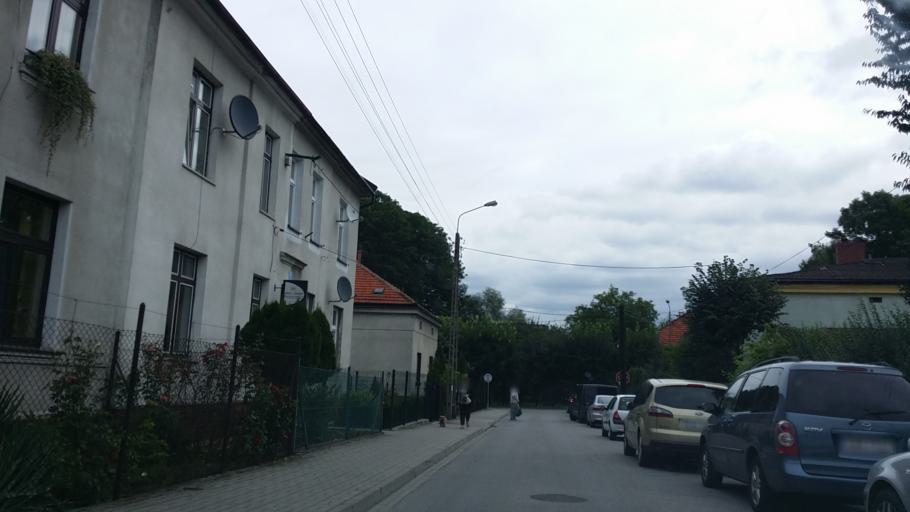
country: PL
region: Lesser Poland Voivodeship
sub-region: Powiat wadowicki
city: Wadowice
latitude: 49.8845
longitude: 19.4879
